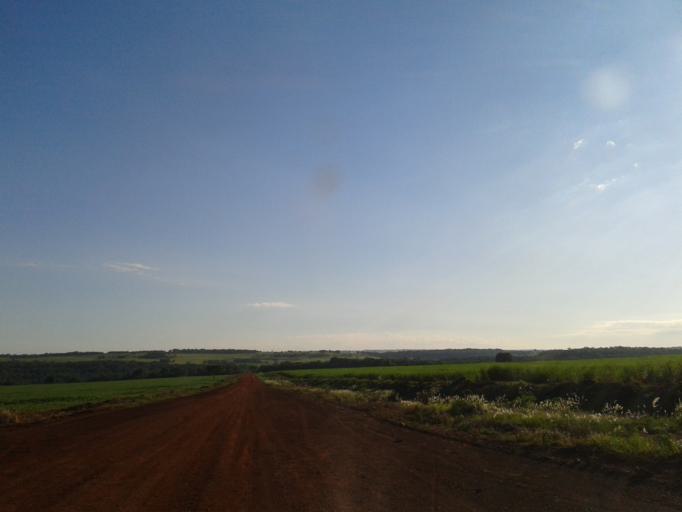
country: BR
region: Minas Gerais
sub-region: Centralina
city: Centralina
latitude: -18.7045
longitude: -49.2869
